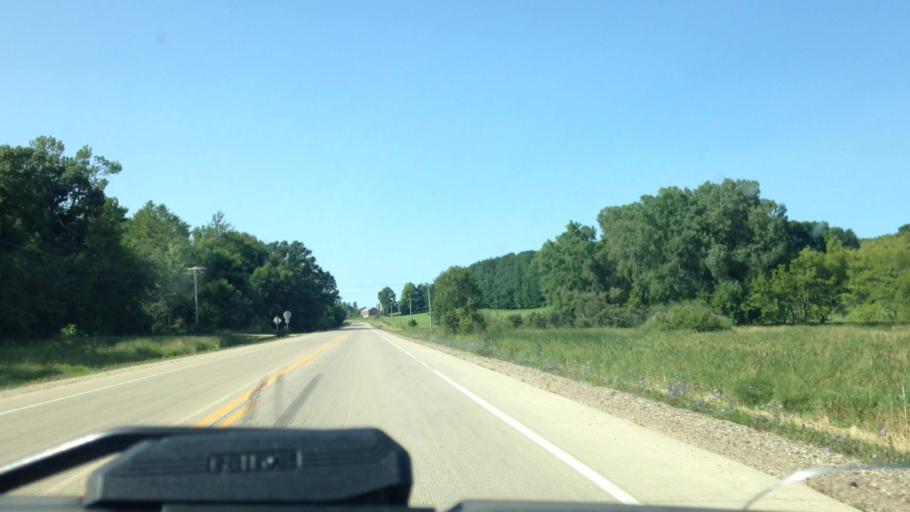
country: US
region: Wisconsin
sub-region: Dodge County
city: Mayville
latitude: 43.4743
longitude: -88.5563
